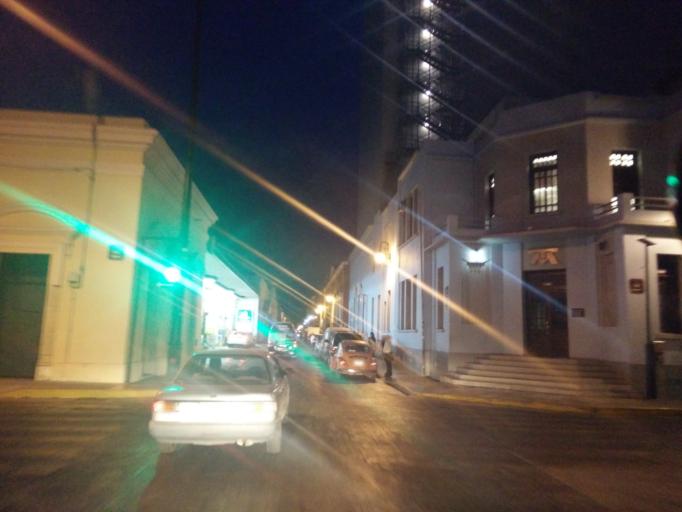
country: MX
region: Yucatan
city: Merida
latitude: 20.9691
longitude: -89.6256
